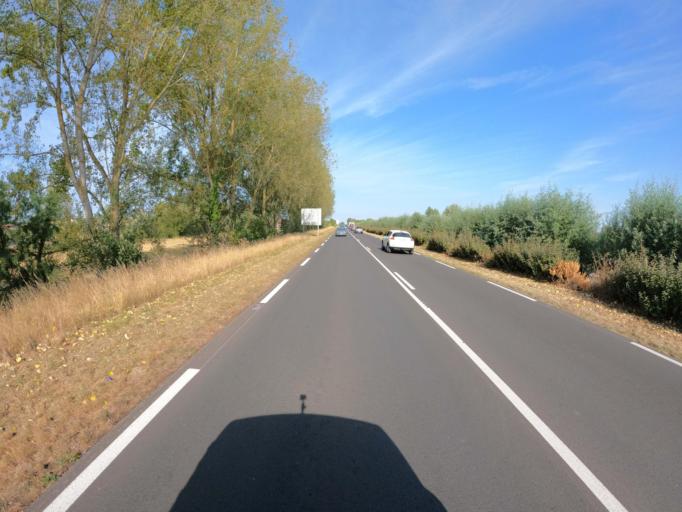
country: FR
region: Pays de la Loire
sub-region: Departement de la Vendee
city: Saint-Jean-de-Monts
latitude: 46.7987
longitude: -2.0568
